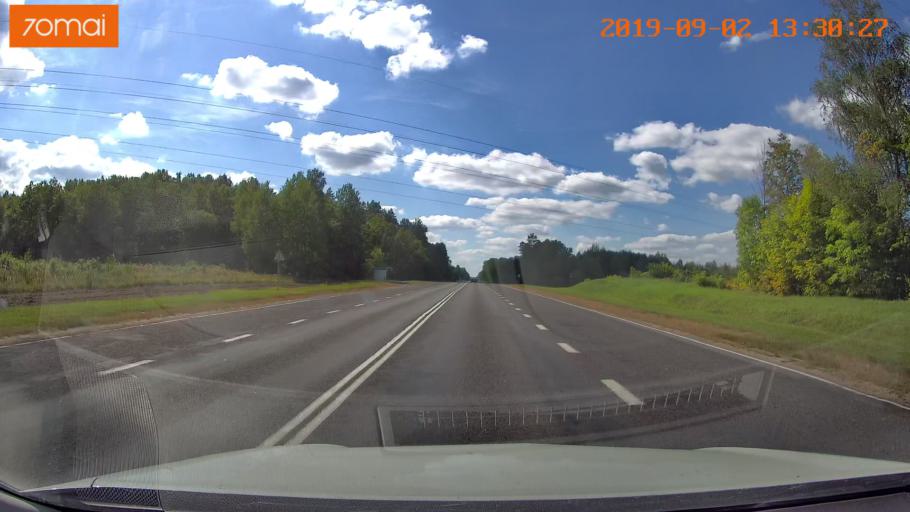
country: BY
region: Mogilev
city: Horad Krychaw
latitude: 53.6622
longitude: 31.6335
